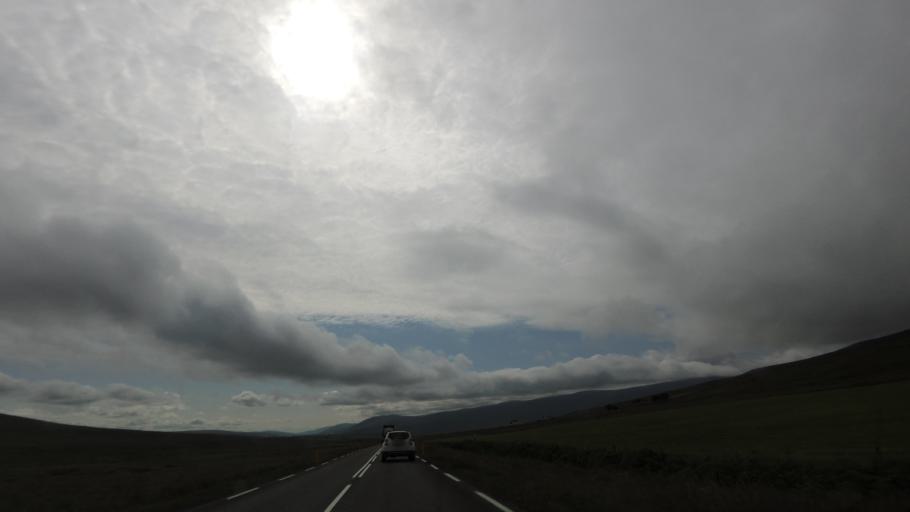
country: IS
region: Northeast
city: Laugar
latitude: 65.7407
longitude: -17.5917
